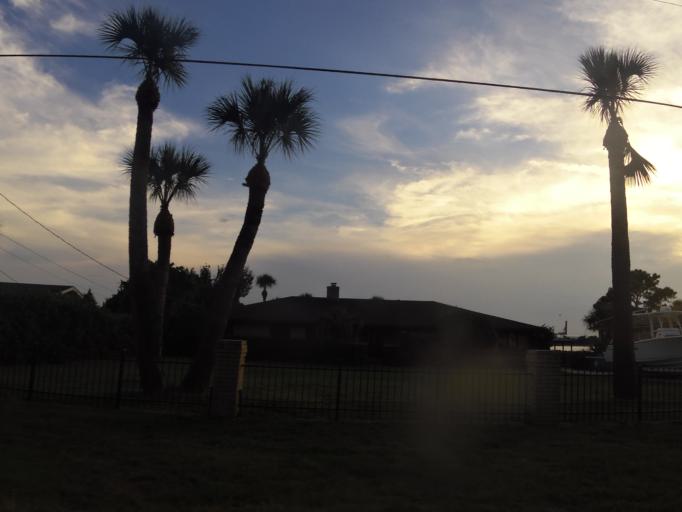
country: US
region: Florida
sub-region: Duval County
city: Atlantic Beach
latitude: 30.3975
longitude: -81.5043
